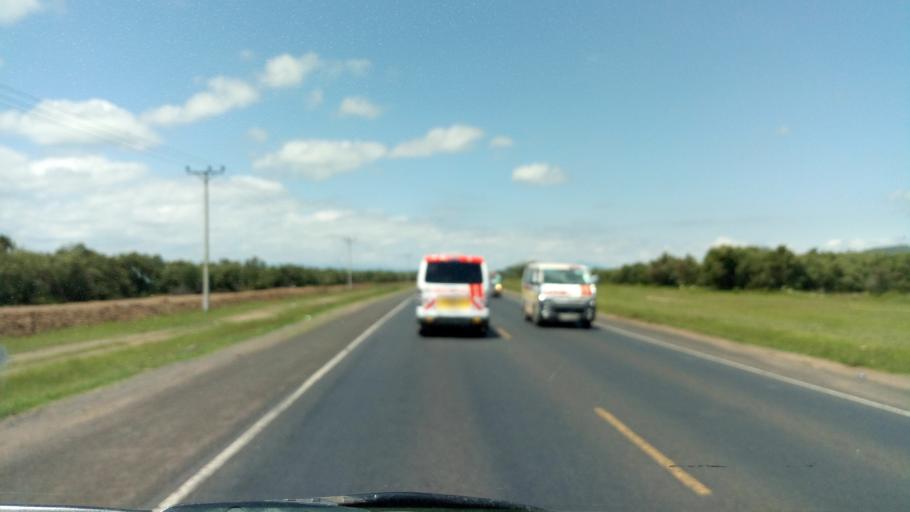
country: KE
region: Nakuru
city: Naivasha
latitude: -0.5538
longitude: 36.3493
